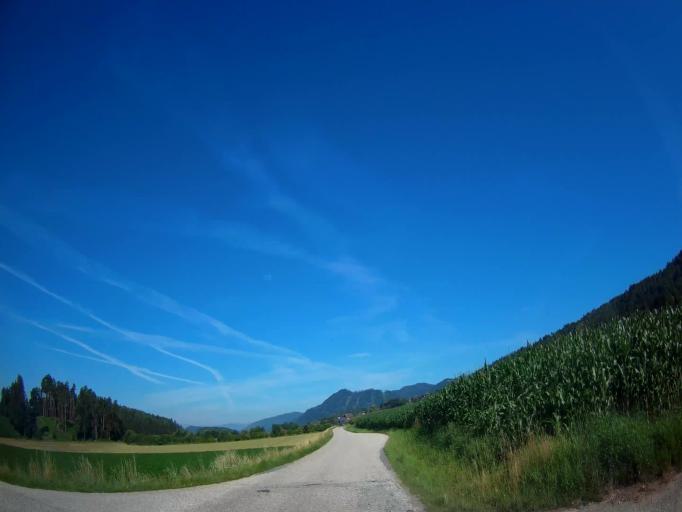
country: AT
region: Carinthia
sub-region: Politischer Bezirk Klagenfurt Land
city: Poggersdorf
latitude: 46.6735
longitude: 14.5232
